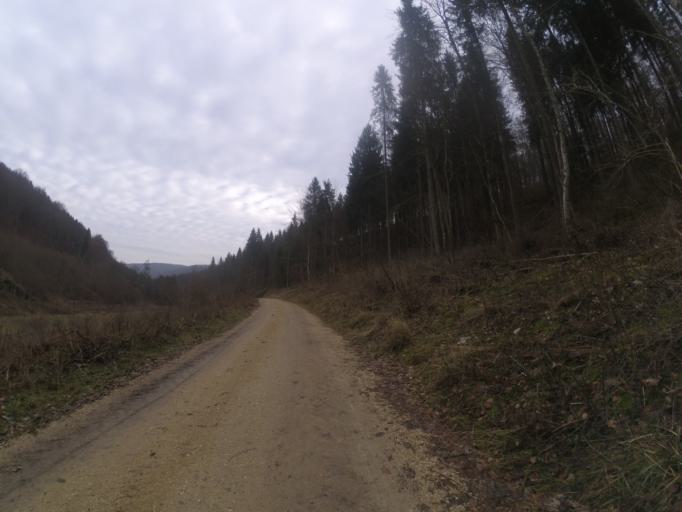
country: DE
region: Baden-Wuerttemberg
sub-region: Tuebingen Region
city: Mehrstetten
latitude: 48.3575
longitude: 9.5801
